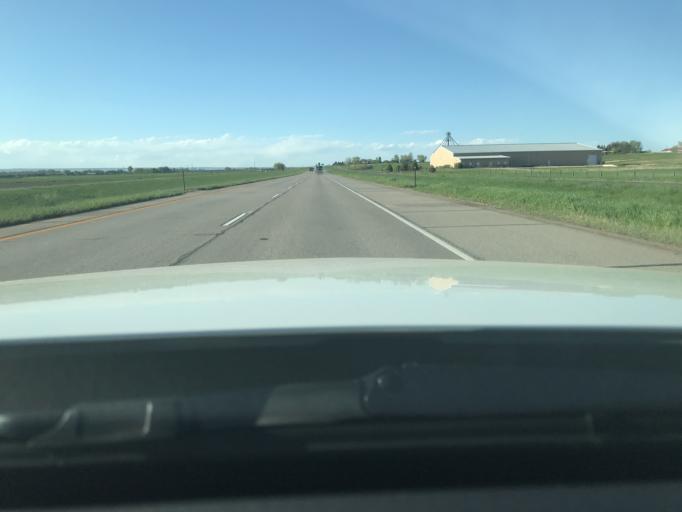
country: US
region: Colorado
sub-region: Larimer County
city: Wellington
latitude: 40.7279
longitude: -104.9933
